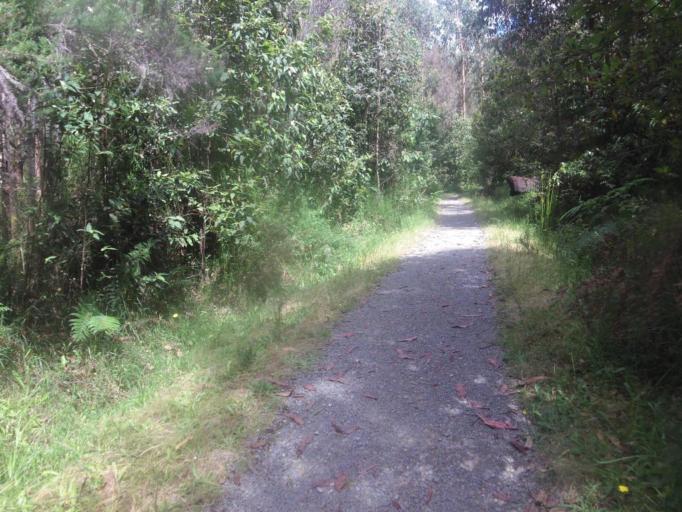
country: AU
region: Victoria
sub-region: Yarra Ranges
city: Millgrove
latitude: -37.5190
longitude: 145.7619
